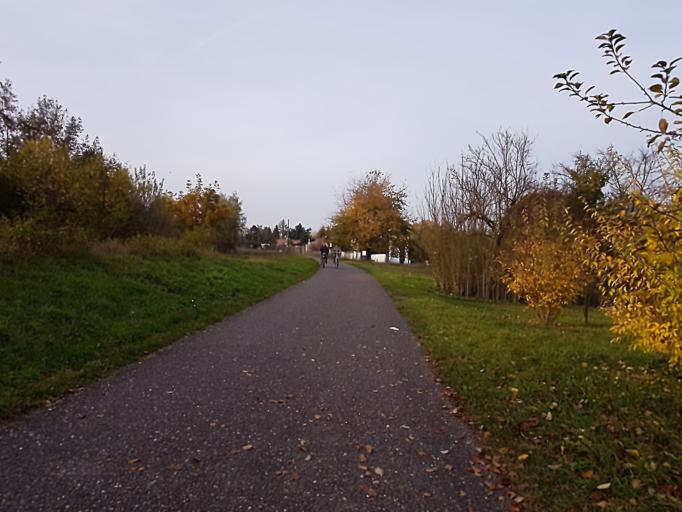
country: DE
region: Bavaria
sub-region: Regierungsbezirk Unterfranken
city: Niedernberg
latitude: 49.8974
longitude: 9.1442
